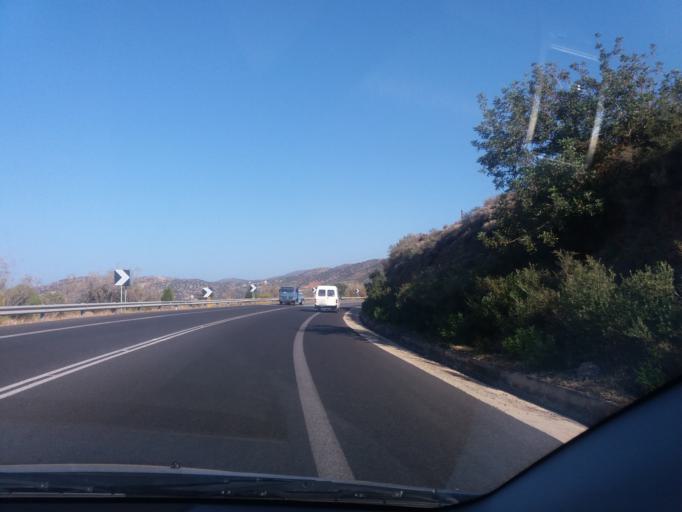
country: GR
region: Crete
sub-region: Nomos Lasithiou
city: Sision
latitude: 35.2930
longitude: 25.5169
